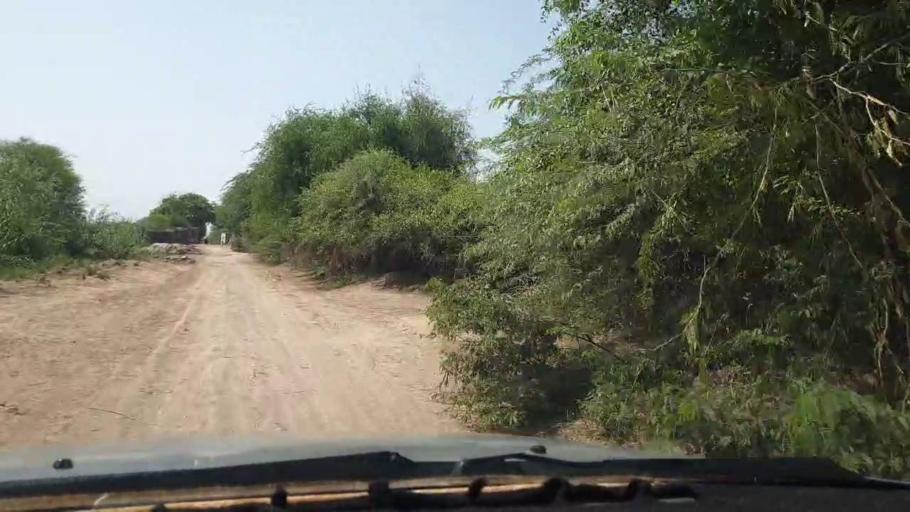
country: PK
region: Sindh
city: Tando Ghulam Ali
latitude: 25.1435
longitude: 68.7883
